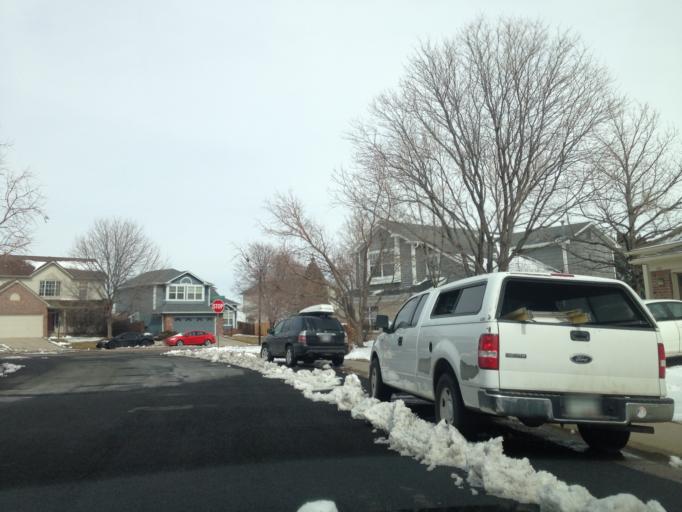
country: US
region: Colorado
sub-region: Boulder County
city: Lafayette
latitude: 39.9753
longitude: -105.0943
